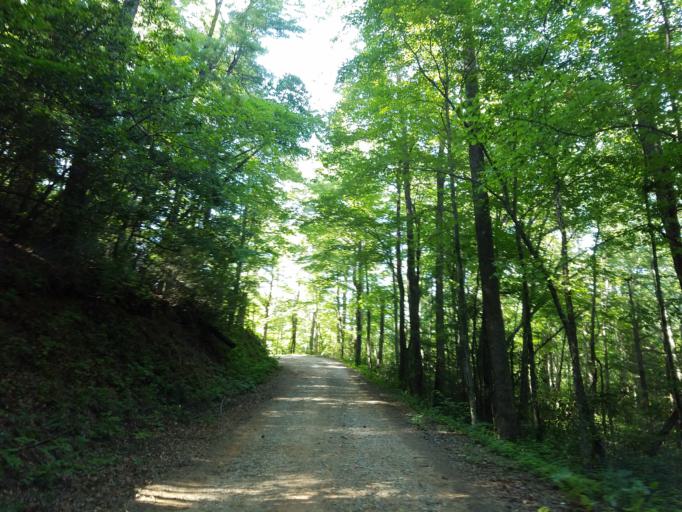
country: US
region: Georgia
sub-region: Dawson County
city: Dawsonville
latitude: 34.5872
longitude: -84.1965
